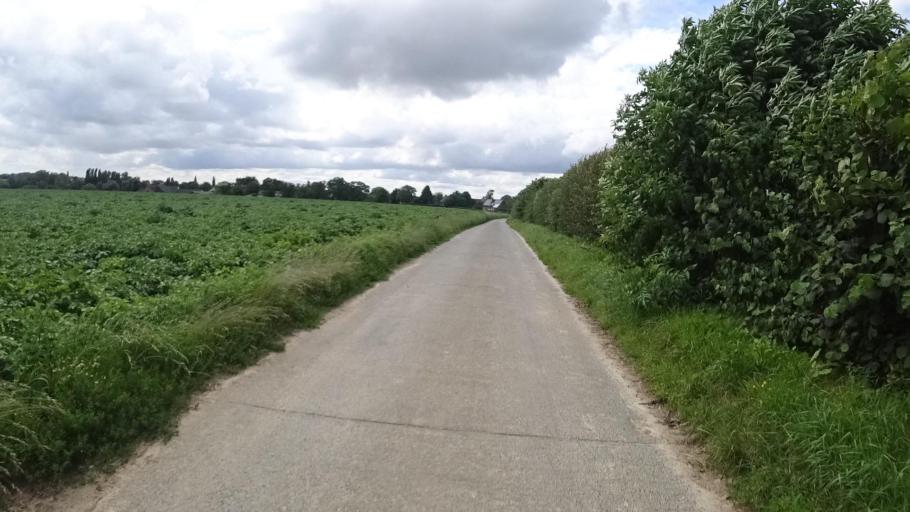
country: BE
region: Wallonia
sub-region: Province du Brabant Wallon
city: Chastre-Villeroux-Blanmont
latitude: 50.5940
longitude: 4.6502
